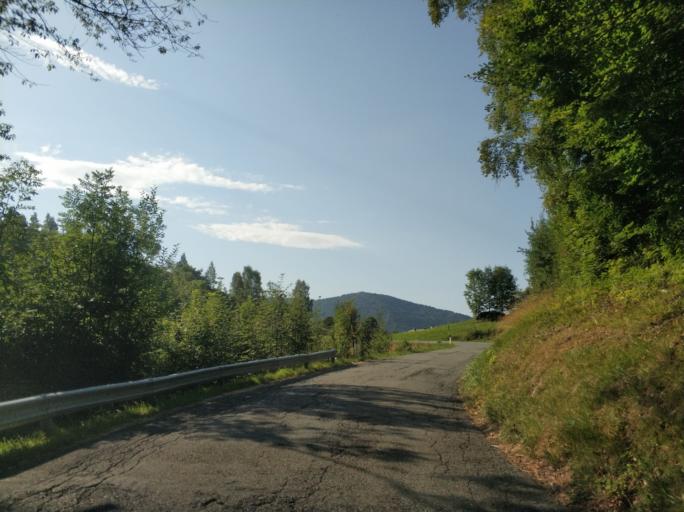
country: IT
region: Piedmont
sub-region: Provincia di Torino
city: Viu
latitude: 45.2079
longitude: 7.3788
